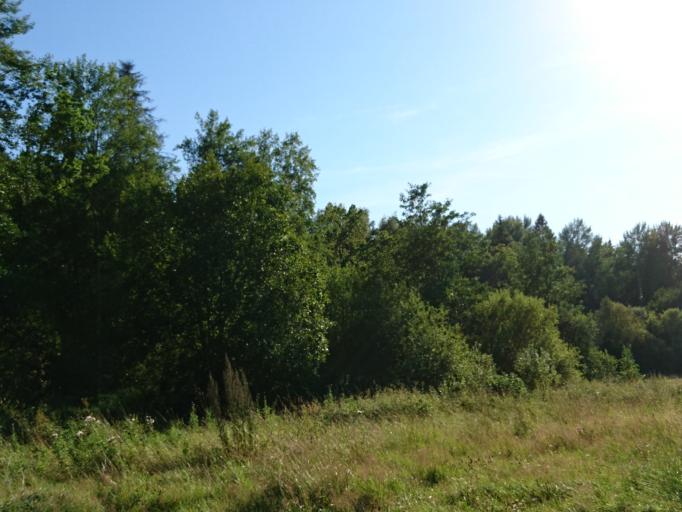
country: SE
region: Stockholm
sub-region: Huddinge Kommun
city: Segeltorp
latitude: 59.2679
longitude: 17.9438
